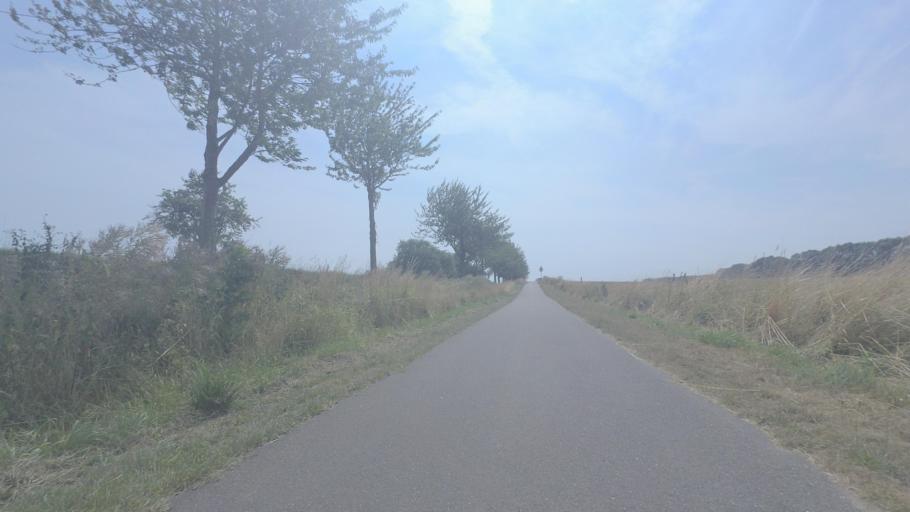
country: DE
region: Mecklenburg-Vorpommern
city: Garz
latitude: 54.3107
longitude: 13.3523
